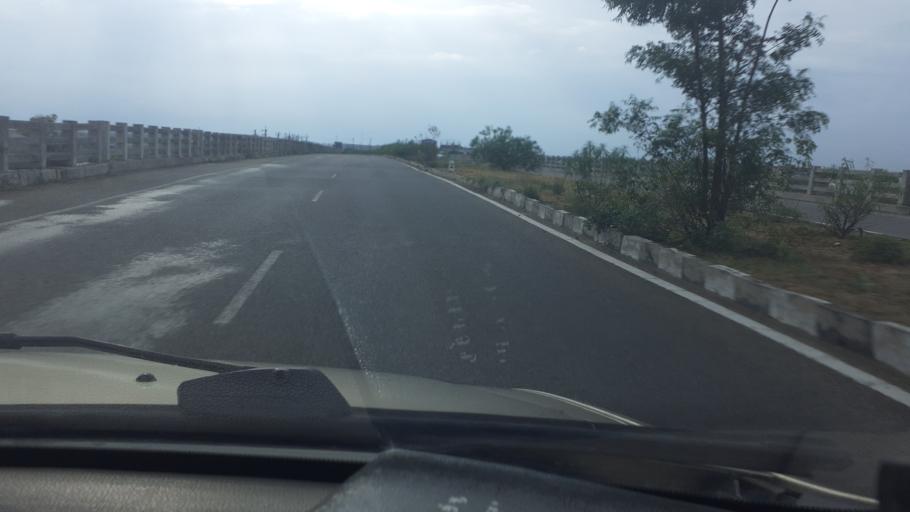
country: IN
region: Tamil Nadu
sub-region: Tirunelveli Kattabo
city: Tirunelveli
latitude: 8.6662
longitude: 77.7395
